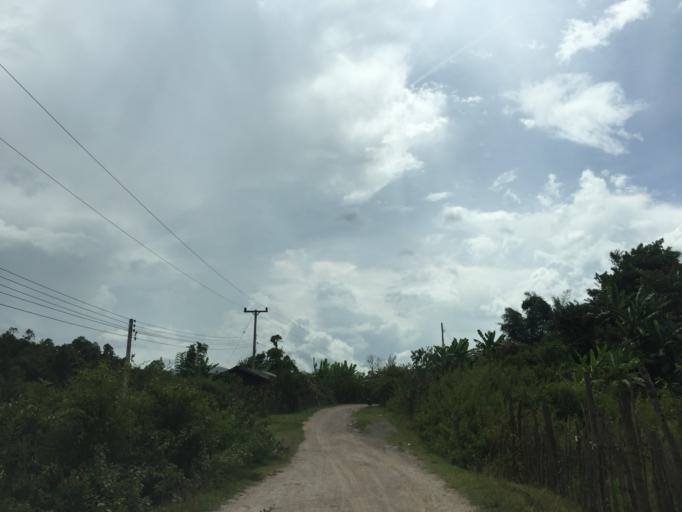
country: LA
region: Xiangkhoang
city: Muang Phonsavan
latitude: 19.3409
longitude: 103.5458
